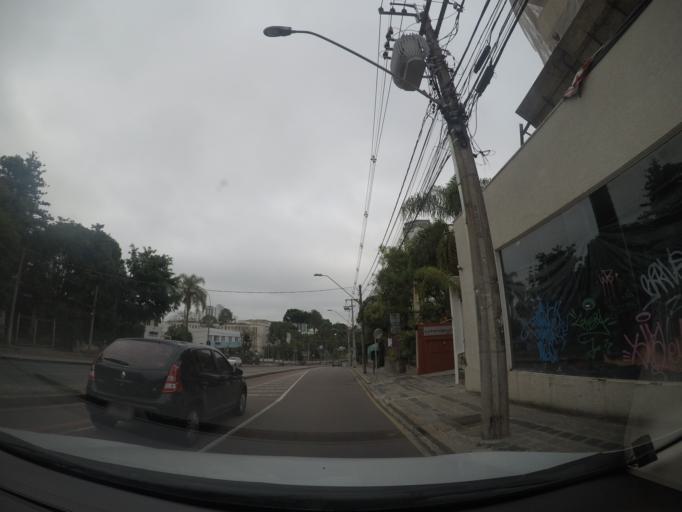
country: BR
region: Parana
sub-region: Curitiba
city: Curitiba
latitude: -25.4217
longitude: -49.2664
